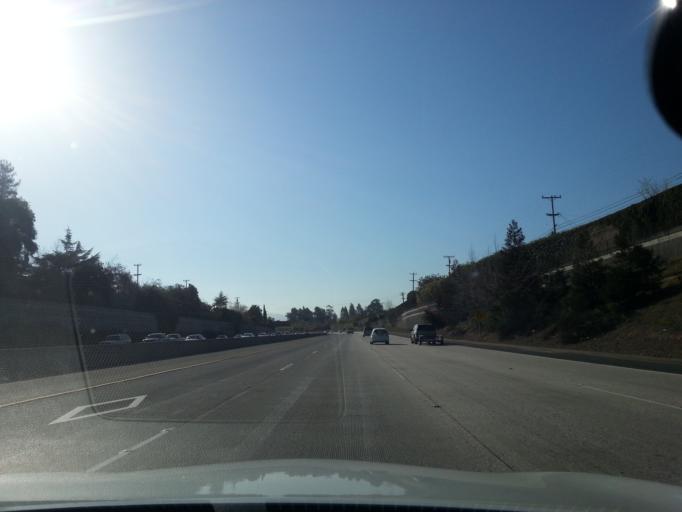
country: US
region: California
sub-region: Santa Clara County
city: Cupertino
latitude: 37.3150
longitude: -122.0466
